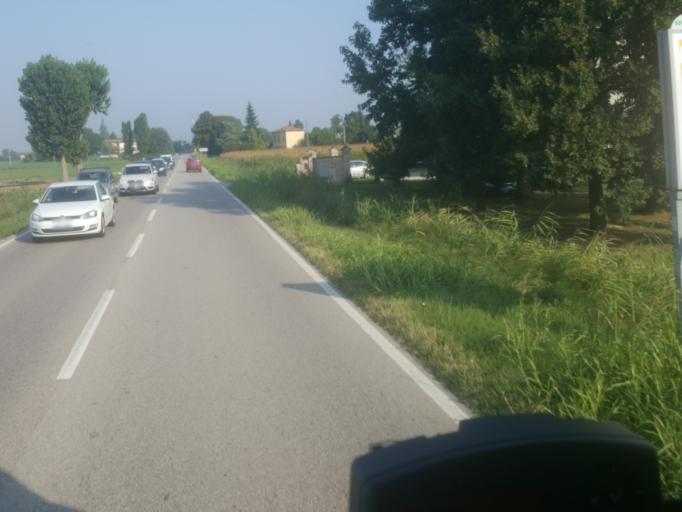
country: IT
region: Emilia-Romagna
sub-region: Provincia di Ravenna
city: Fornace Zarattini
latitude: 44.4413
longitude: 12.1372
